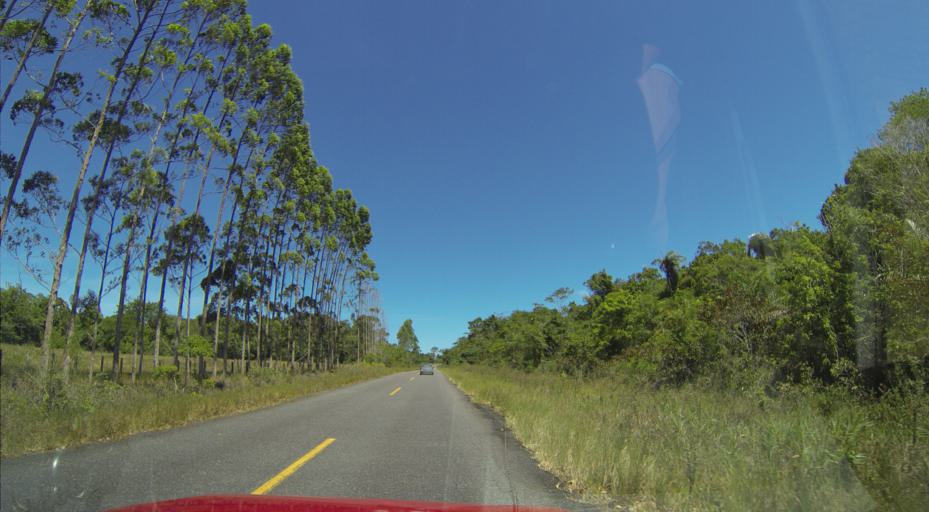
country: BR
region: Bahia
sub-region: Prado
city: Prado
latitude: -17.2741
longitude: -39.3324
